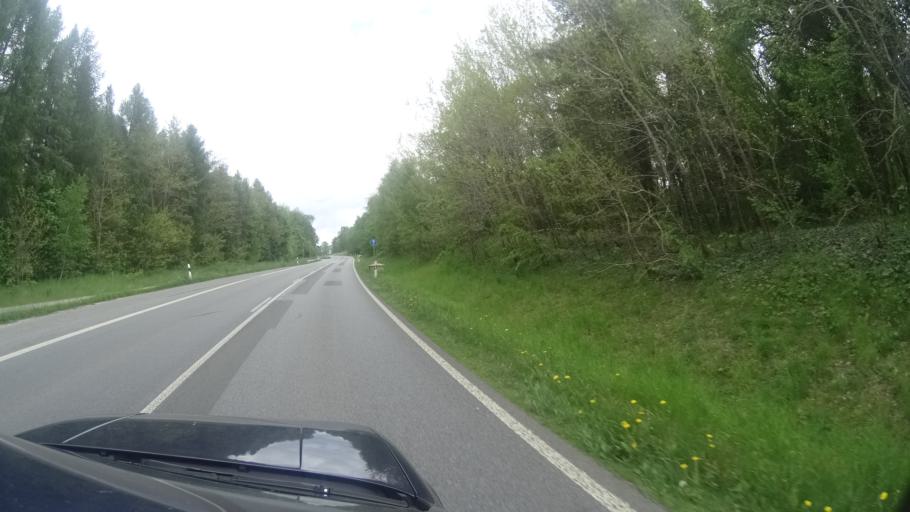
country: DE
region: Mecklenburg-Vorpommern
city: Malchow
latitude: 53.4653
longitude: 12.4283
